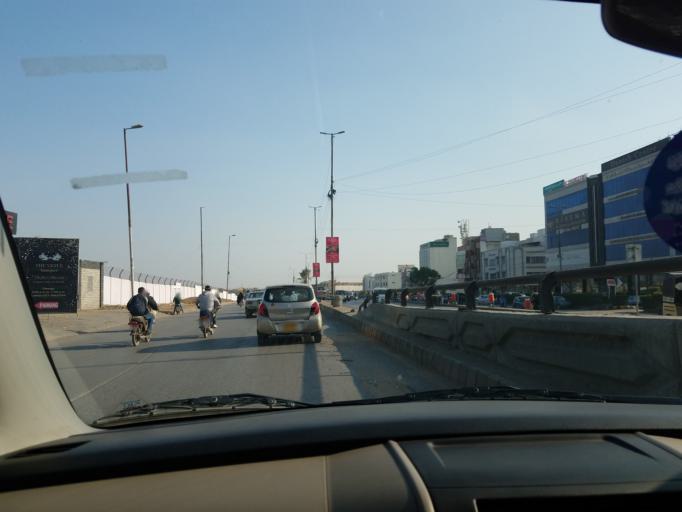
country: PK
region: Sindh
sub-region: Karachi District
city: Karachi
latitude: 24.8981
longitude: 67.1176
